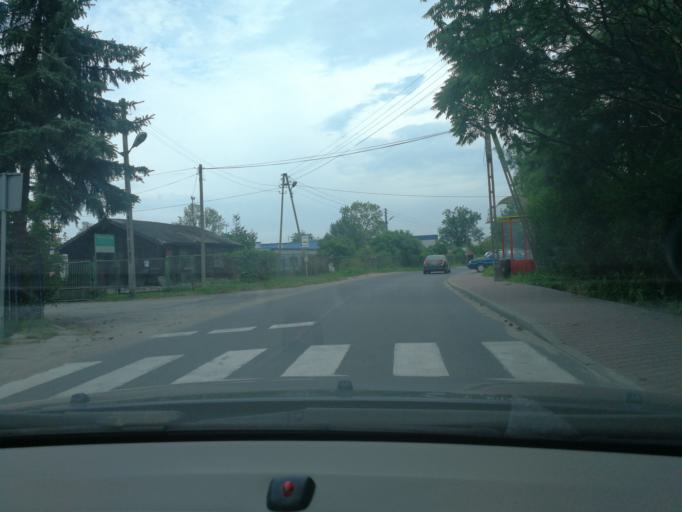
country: PL
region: Masovian Voivodeship
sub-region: Powiat grodziski
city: Grodzisk Mazowiecki
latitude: 52.1307
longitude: 20.5952
